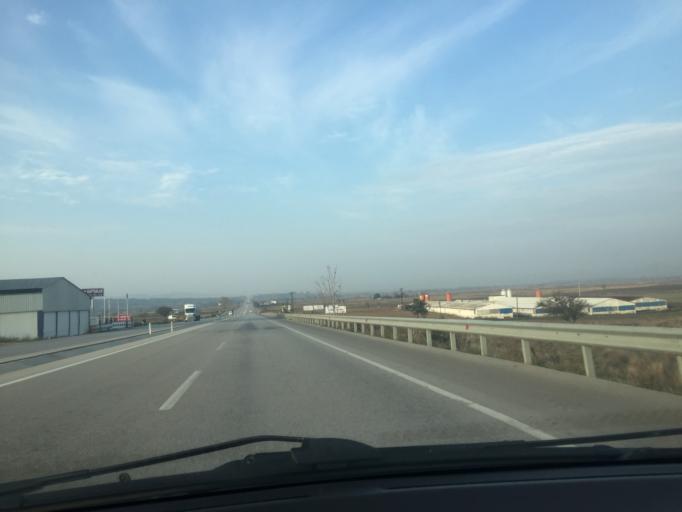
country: TR
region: Canakkale
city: Dimetoka
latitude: 40.2568
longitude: 27.3351
